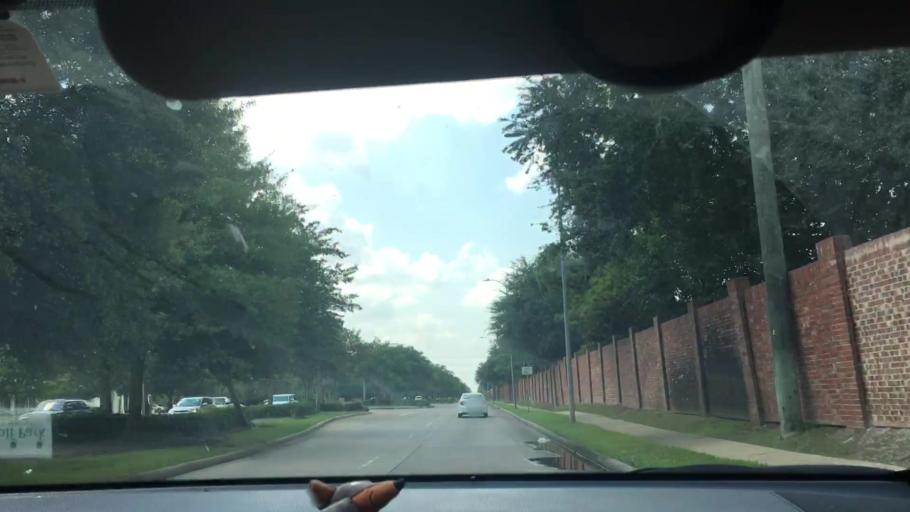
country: US
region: Texas
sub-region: Harris County
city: Bunker Hill Village
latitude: 29.7265
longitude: -95.5717
